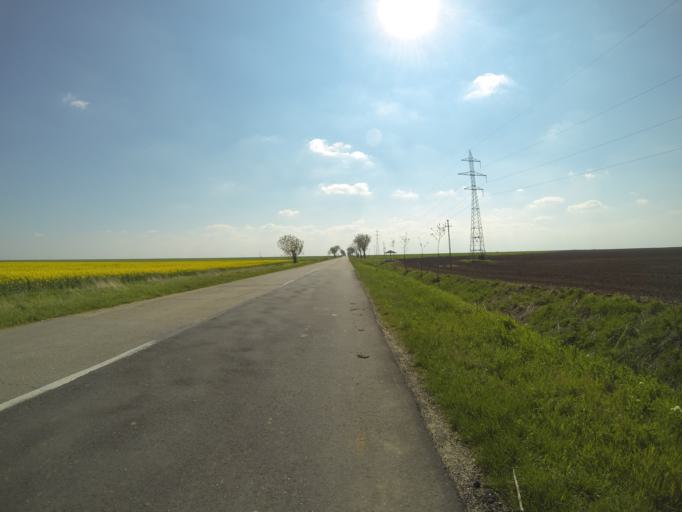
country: RO
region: Mehedinti
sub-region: Comuna Darvari
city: Gemeni
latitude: 44.1408
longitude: 23.0907
